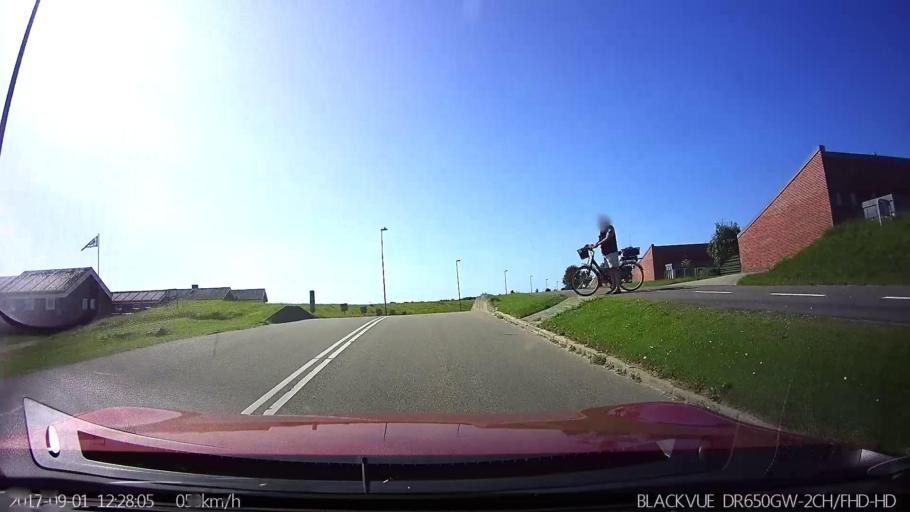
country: DK
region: South Denmark
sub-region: Fano Kommune
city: Nordby
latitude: 55.4437
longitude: 8.4059
